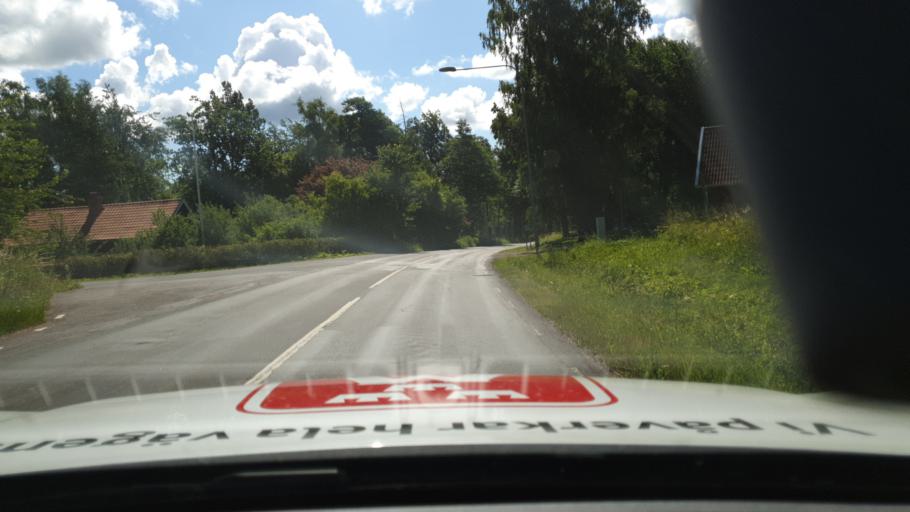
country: SE
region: Vaestra Goetaland
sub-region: Skovde Kommun
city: Stopen
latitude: 58.5036
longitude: 13.8111
